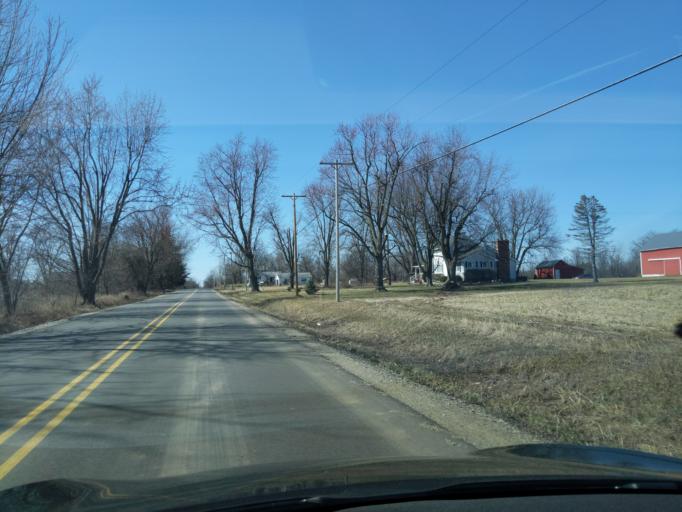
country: US
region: Michigan
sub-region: Eaton County
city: Grand Ledge
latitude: 42.7265
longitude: -84.7900
